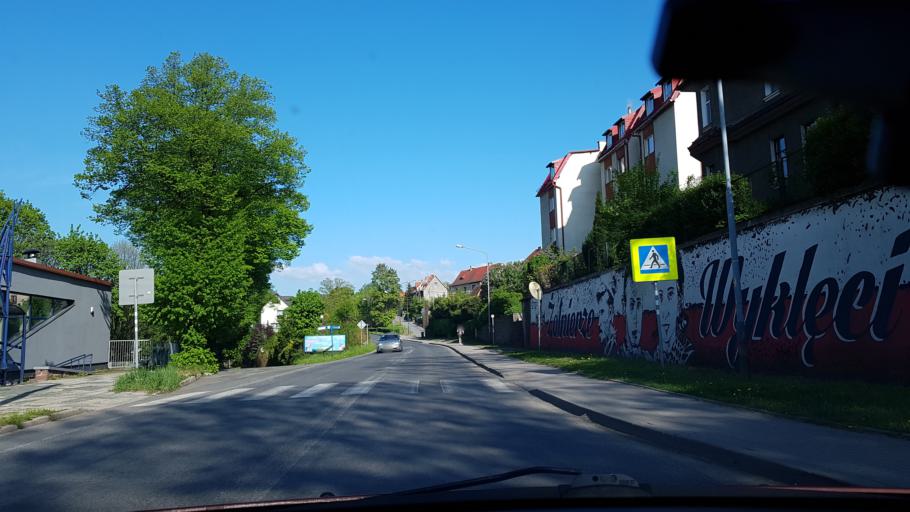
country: PL
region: Lower Silesian Voivodeship
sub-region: Powiat klodzki
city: Nowa Ruda
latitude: 50.5797
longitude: 16.5089
